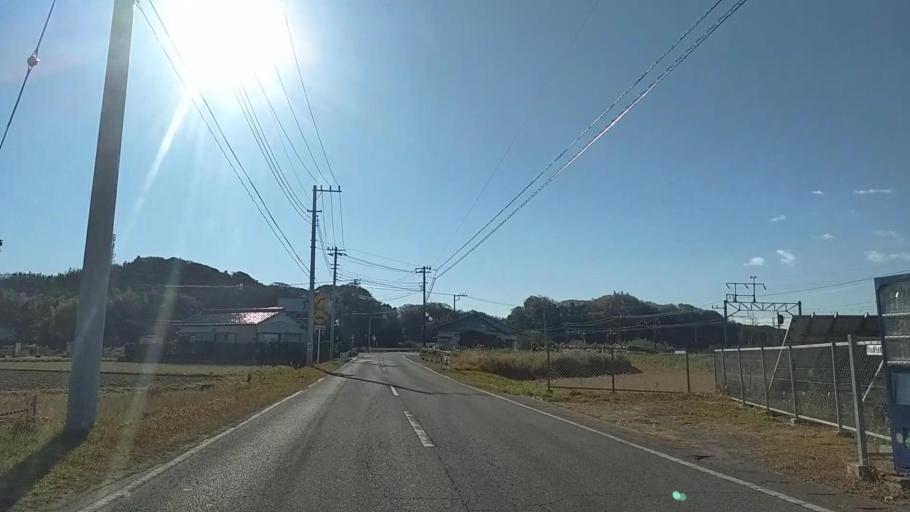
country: JP
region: Chiba
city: Kimitsu
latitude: 35.2595
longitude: 139.8769
